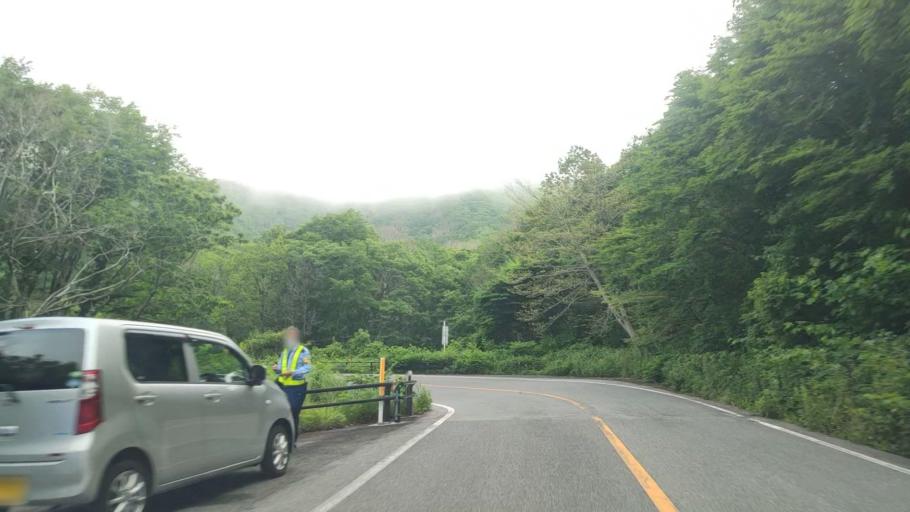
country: JP
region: Tottori
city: Yonago
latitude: 35.3328
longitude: 133.5722
